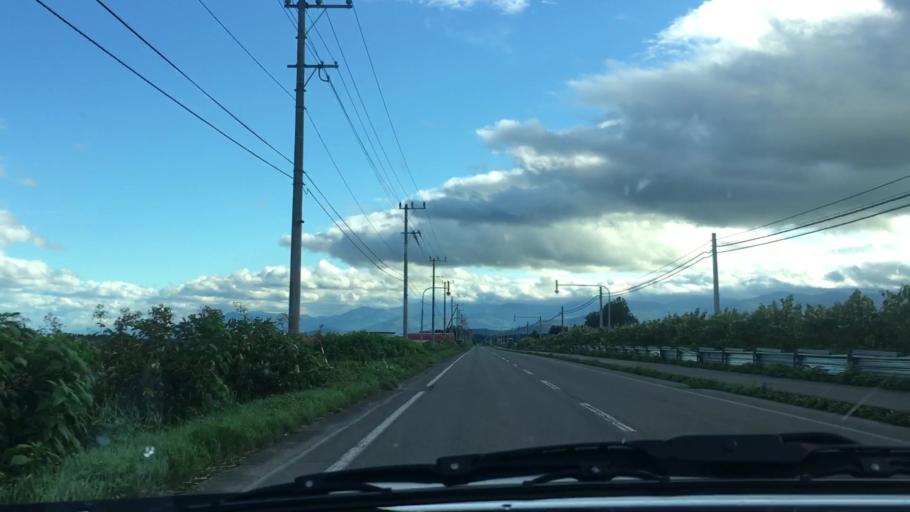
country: JP
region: Hokkaido
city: Otofuke
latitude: 43.1524
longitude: 142.9008
